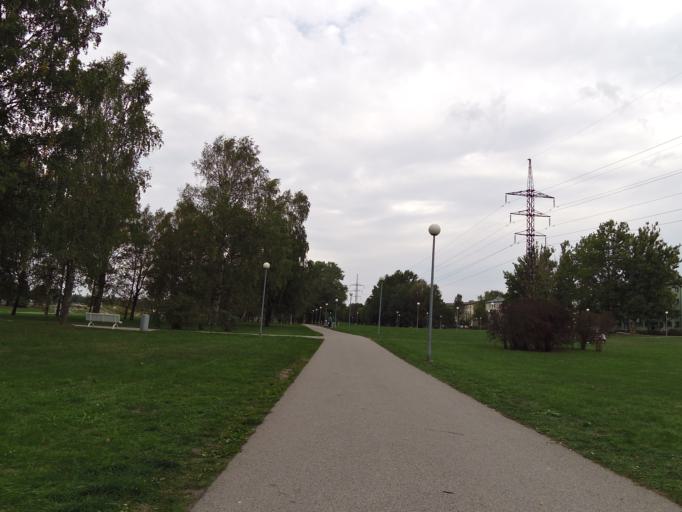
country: EE
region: Harju
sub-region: Tallinna linn
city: Tallinn
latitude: 59.4448
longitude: 24.6859
